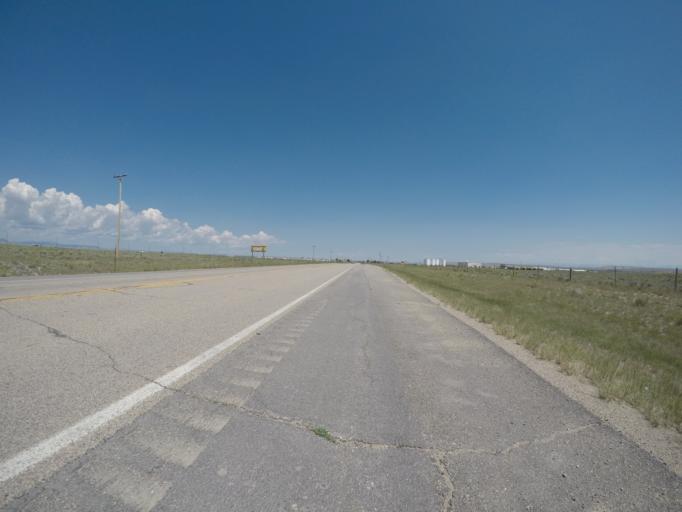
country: US
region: Wyoming
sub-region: Sublette County
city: Marbleton
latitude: 42.5051
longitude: -110.1050
